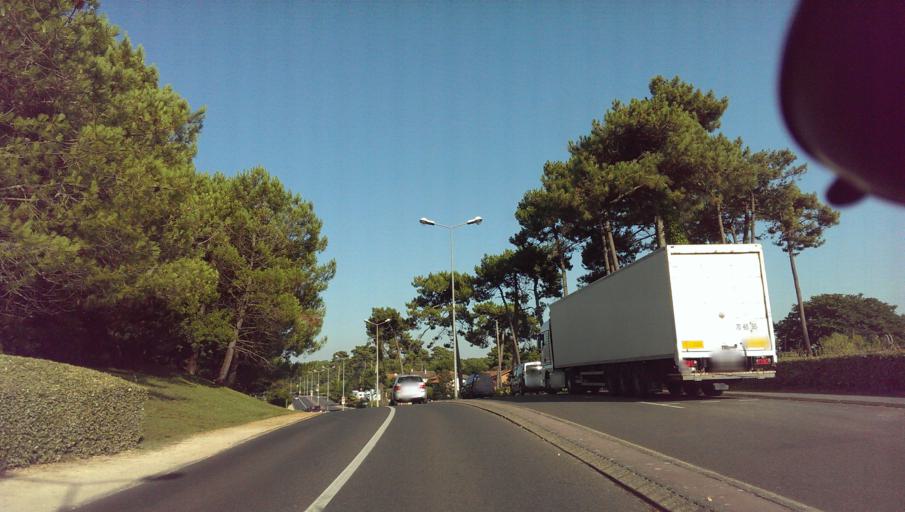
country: FR
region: Aquitaine
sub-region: Departement des Landes
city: Mimizan
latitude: 44.2120
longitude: -1.2886
